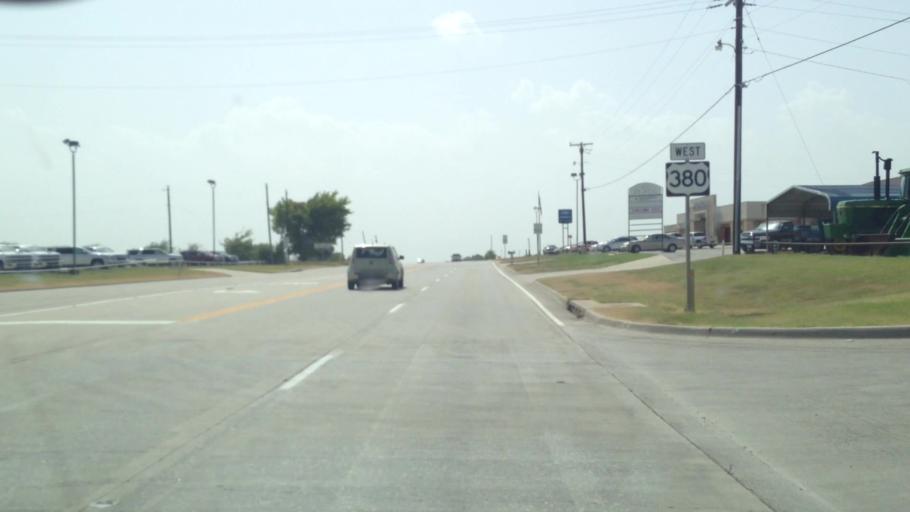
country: US
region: Texas
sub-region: Collin County
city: Farmersville
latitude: 33.1584
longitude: -96.3793
